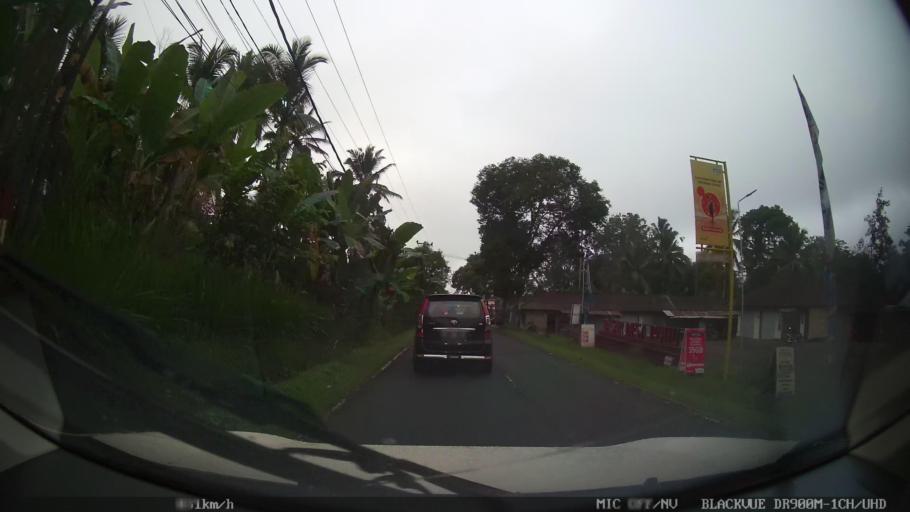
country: ID
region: Bali
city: Banjar Ponggang
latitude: -8.3861
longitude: 115.2623
